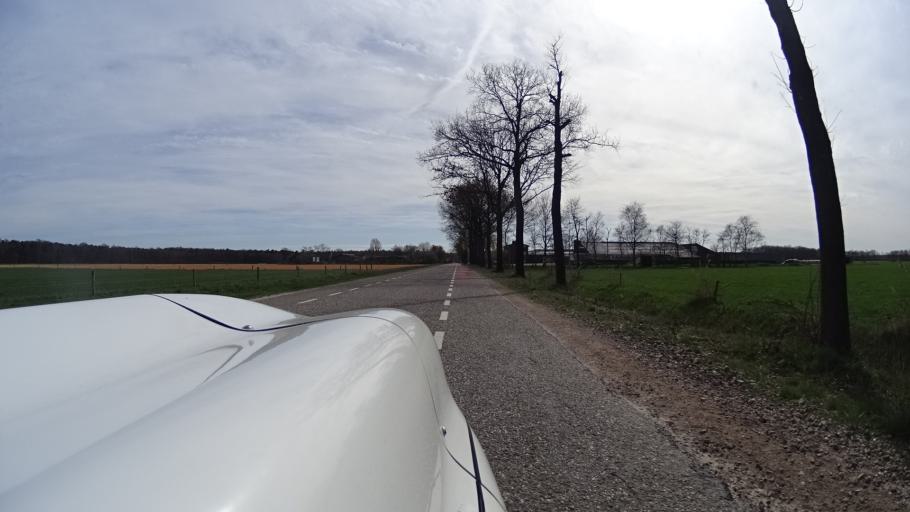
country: NL
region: Limburg
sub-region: Gemeente Venlo
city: Arcen
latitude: 51.5191
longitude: 6.2015
